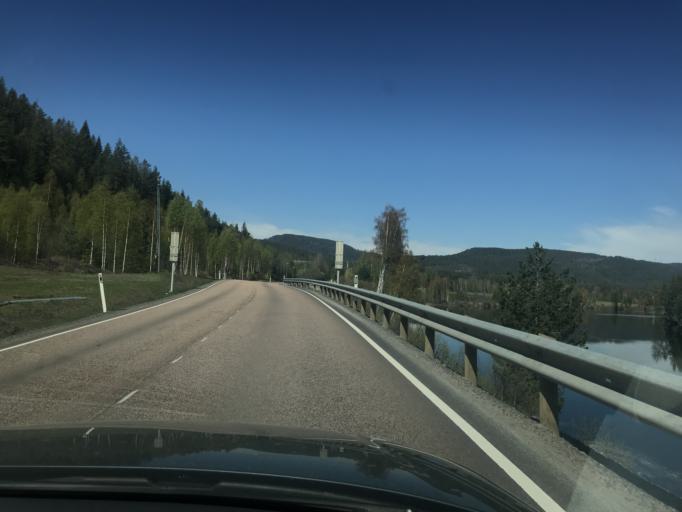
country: NO
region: Buskerud
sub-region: Kongsberg
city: Kongsberg
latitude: 59.6999
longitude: 9.6182
